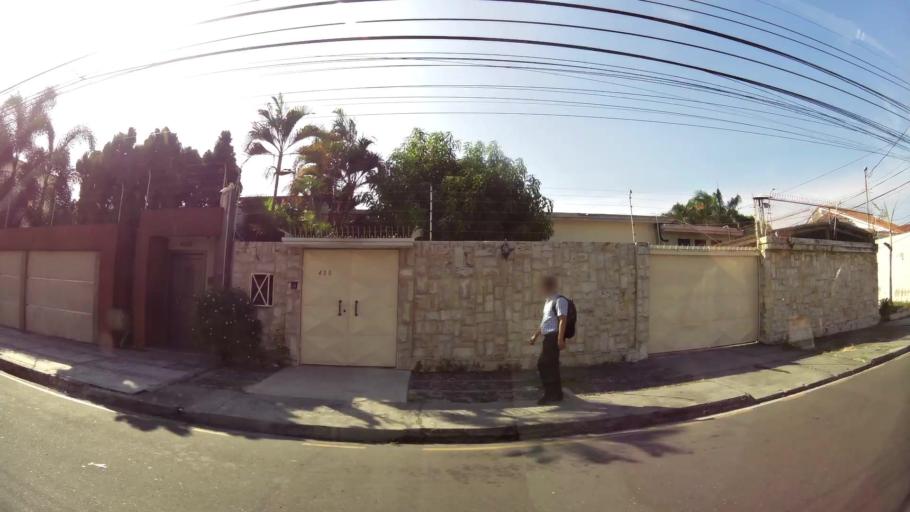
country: EC
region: Guayas
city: Guayaquil
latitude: -2.1700
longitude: -79.9036
